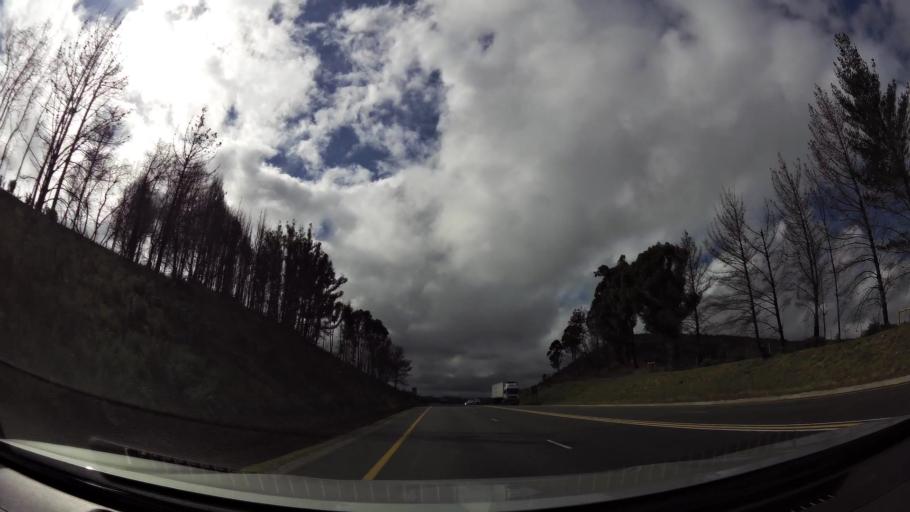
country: ZA
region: Western Cape
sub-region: Eden District Municipality
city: Knysna
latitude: -34.0368
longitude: 23.1228
